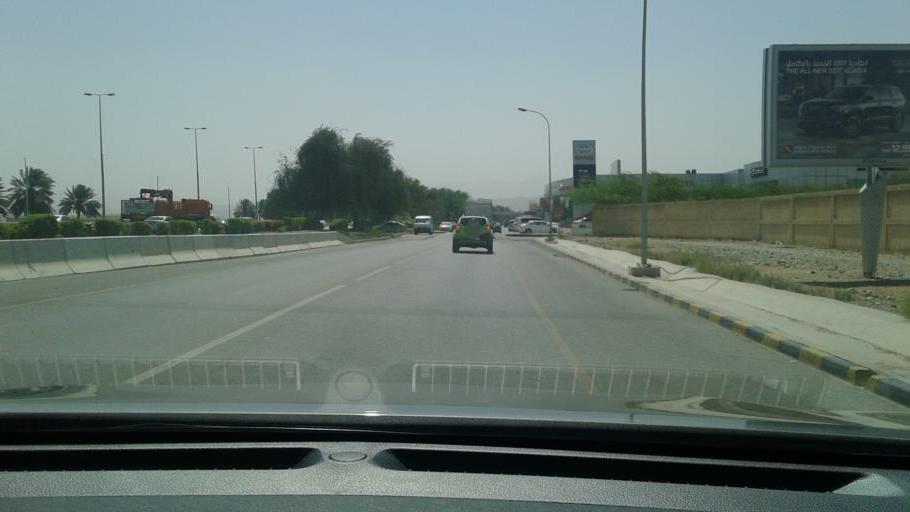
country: OM
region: Muhafazat Masqat
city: As Sib al Jadidah
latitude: 23.6071
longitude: 58.2476
